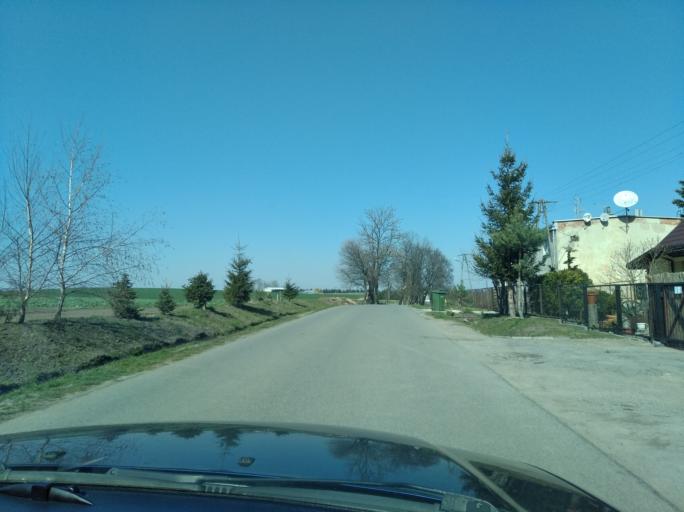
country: PL
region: Subcarpathian Voivodeship
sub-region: Powiat jaroslawski
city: Pawlosiow
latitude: 49.9544
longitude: 22.6507
